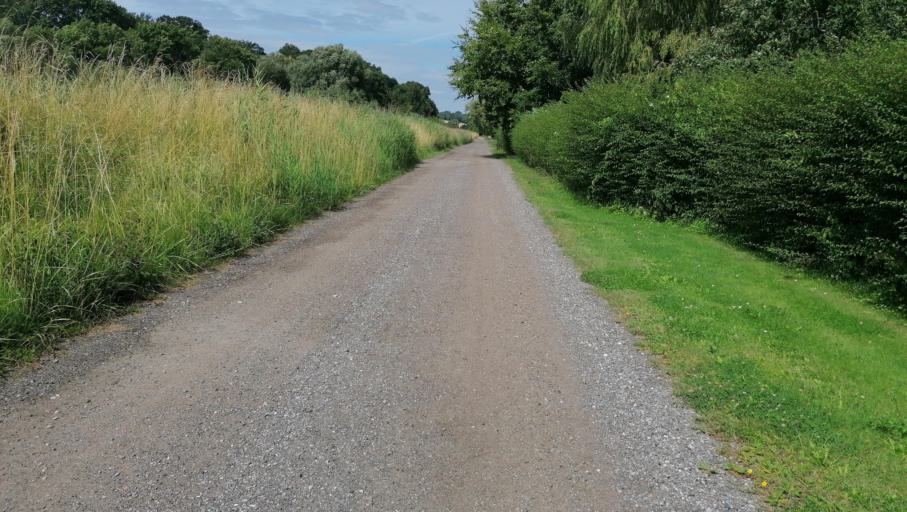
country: DK
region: Zealand
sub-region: Odsherred Kommune
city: Horve
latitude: 55.7758
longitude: 11.4218
